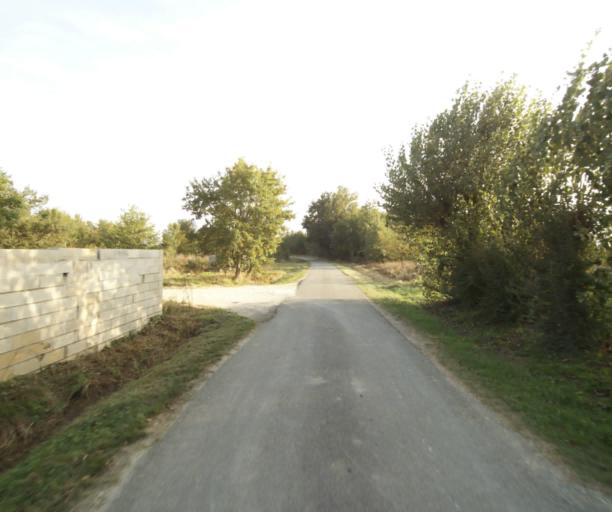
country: FR
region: Midi-Pyrenees
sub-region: Departement du Tarn-et-Garonne
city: Campsas
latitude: 43.9012
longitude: 1.3415
